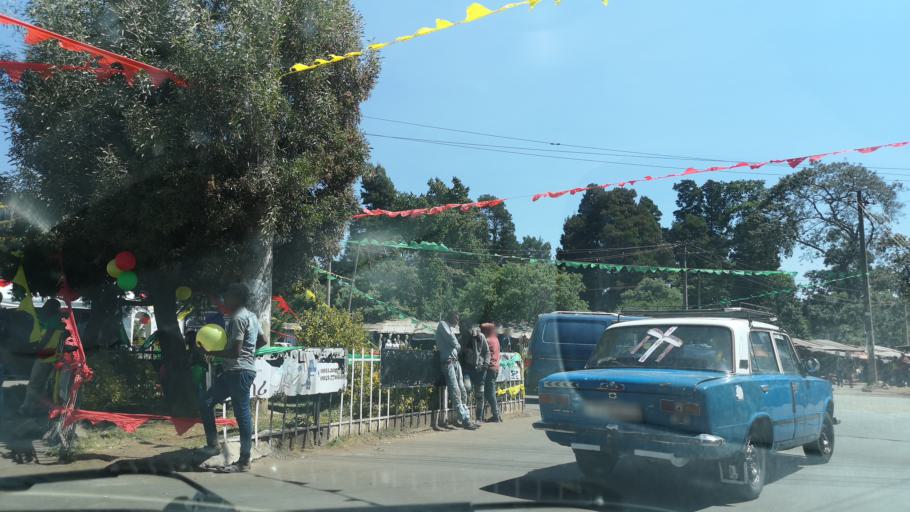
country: ET
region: Adis Abeba
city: Addis Ababa
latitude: 9.0522
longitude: 38.7499
